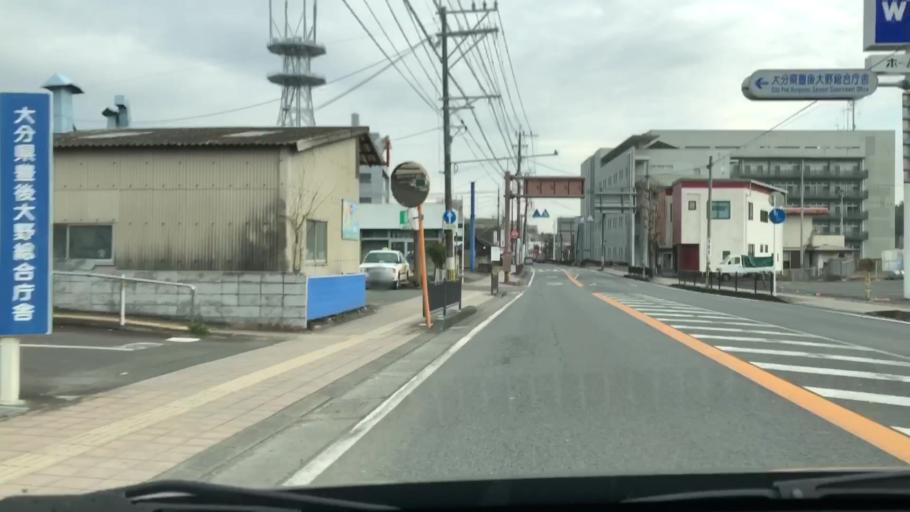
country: JP
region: Oita
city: Takedamachi
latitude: 32.9766
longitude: 131.5826
